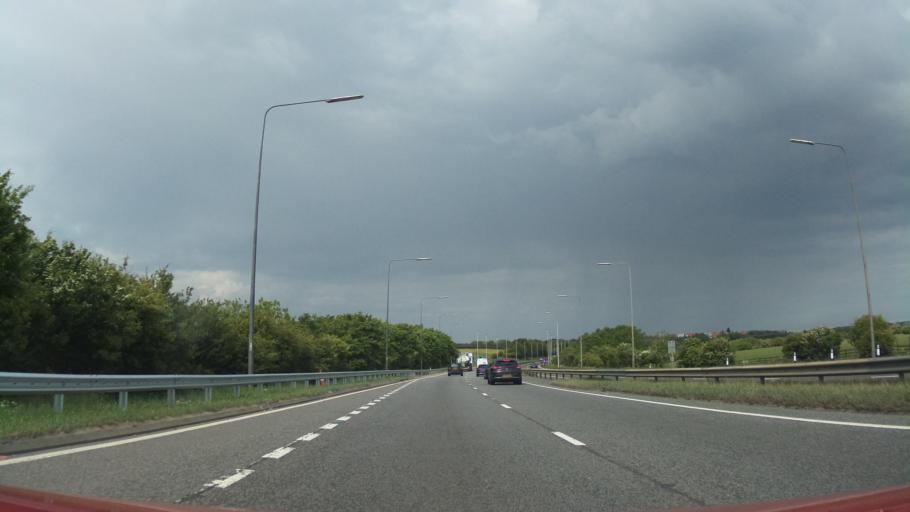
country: GB
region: England
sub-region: County Durham
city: Shotton
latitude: 54.7906
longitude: -1.3664
